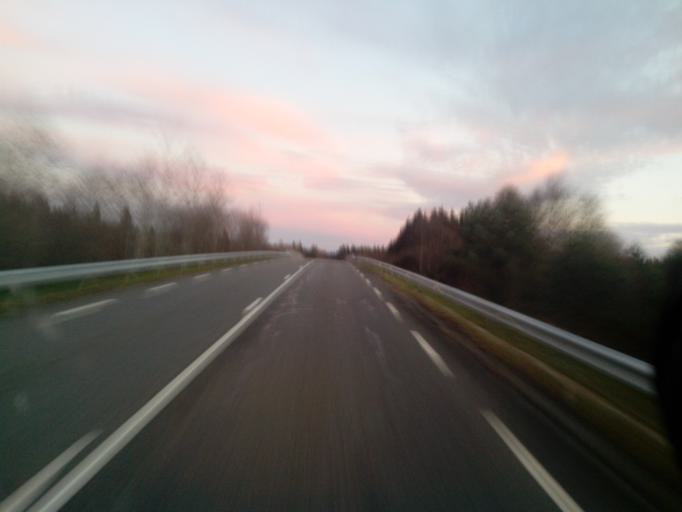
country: FR
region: Limousin
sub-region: Departement de la Correze
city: Meymac
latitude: 45.5081
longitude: 2.2014
